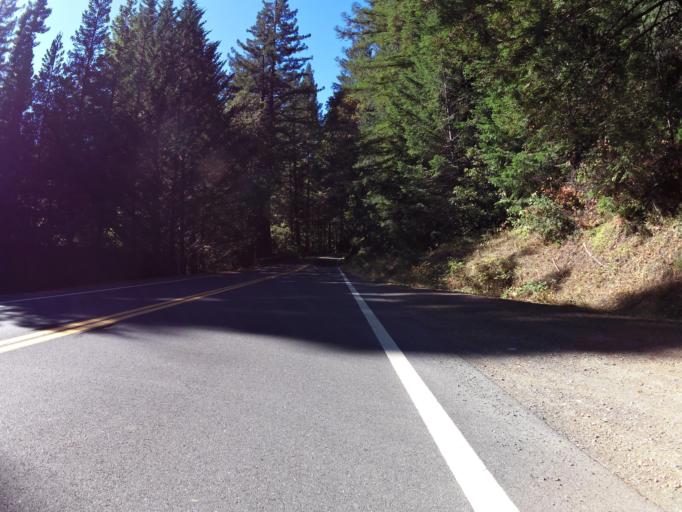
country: US
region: California
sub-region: Humboldt County
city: Redway
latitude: 39.8630
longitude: -123.7247
